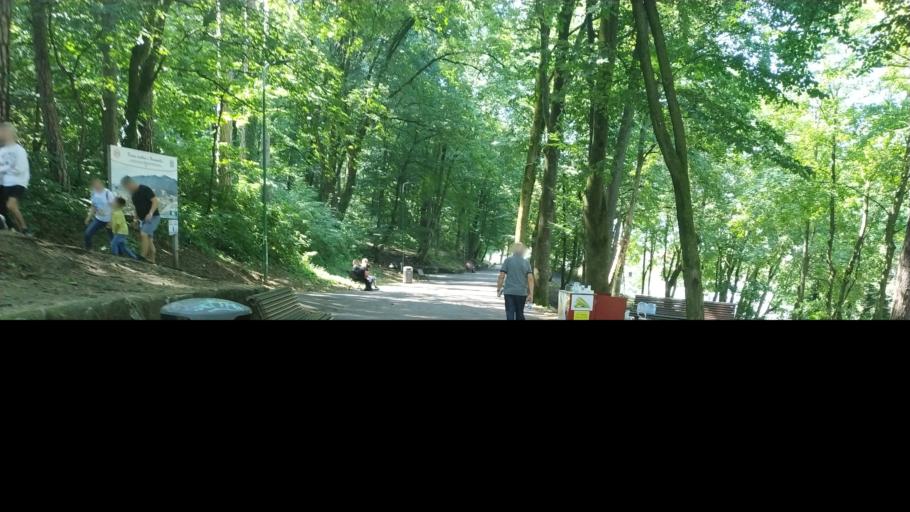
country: RO
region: Brasov
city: Brasov
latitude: 45.6390
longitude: 25.5928
